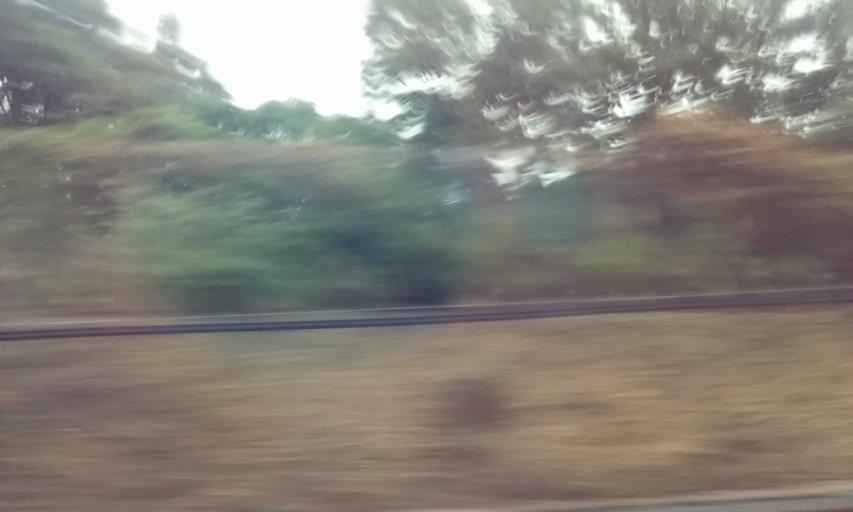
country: JP
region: Hyogo
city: Aioi
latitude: 34.8181
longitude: 134.4974
